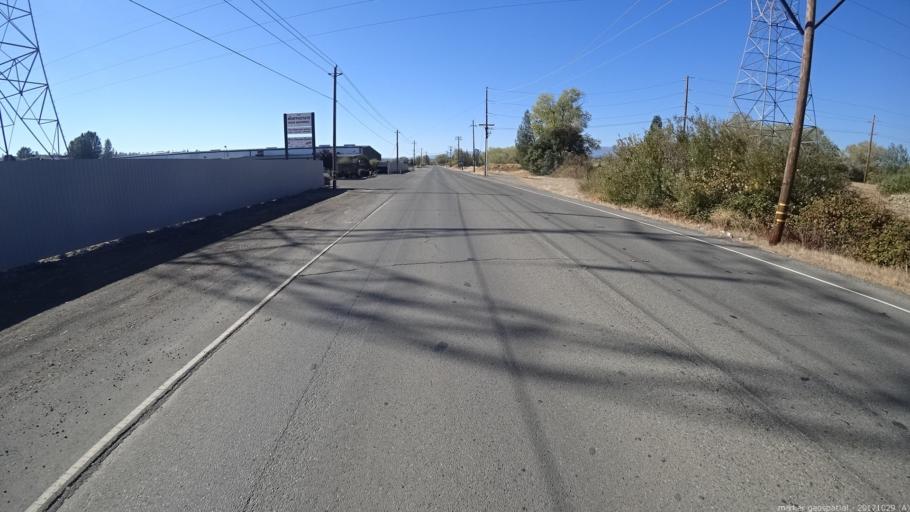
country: US
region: California
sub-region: Shasta County
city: Redding
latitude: 40.5026
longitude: -122.4268
